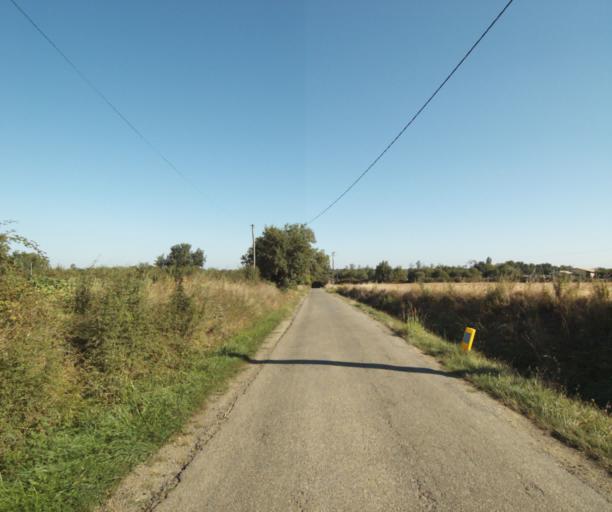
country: FR
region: Midi-Pyrenees
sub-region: Departement du Tarn-et-Garonne
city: Verdun-sur-Garonne
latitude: 43.8574
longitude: 1.2109
